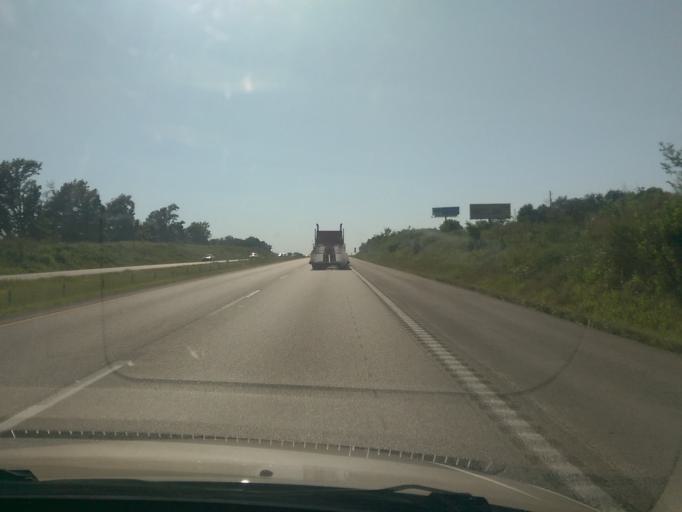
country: US
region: Missouri
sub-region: Saline County
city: Sweet Springs
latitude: 38.9749
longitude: -93.3705
